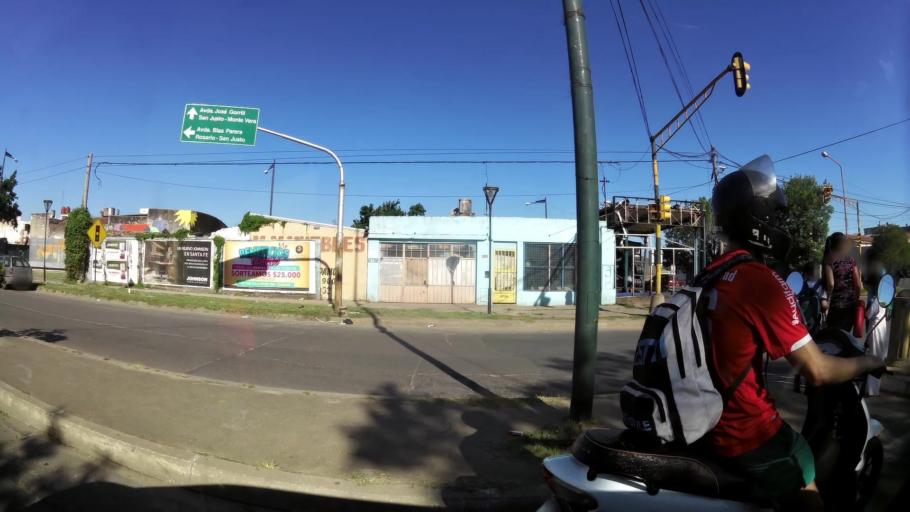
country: AR
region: Santa Fe
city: Santa Fe de la Vera Cruz
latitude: -31.6045
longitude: -60.7029
